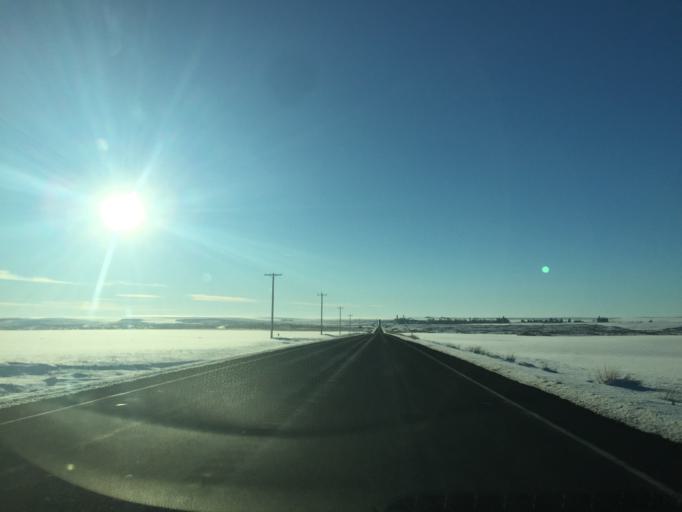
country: US
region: Washington
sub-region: Okanogan County
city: Coulee Dam
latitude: 47.7191
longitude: -118.9014
